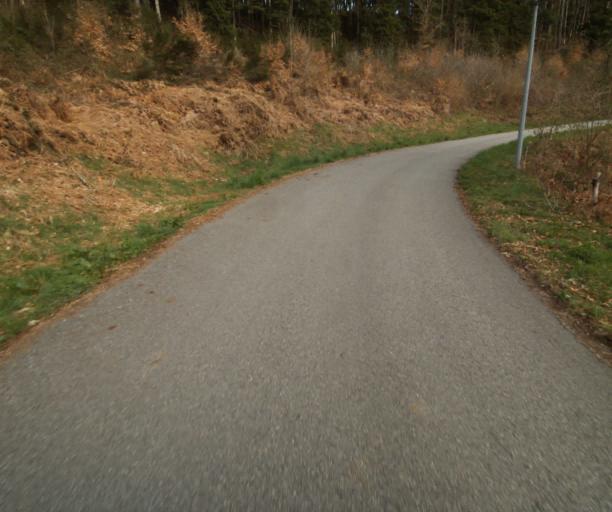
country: FR
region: Limousin
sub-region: Departement de la Correze
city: Correze
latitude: 45.3834
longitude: 1.8767
